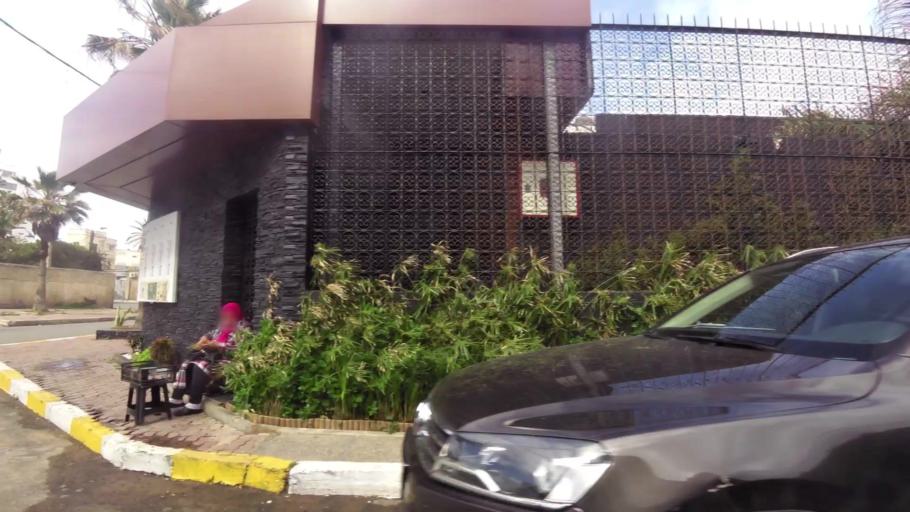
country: MA
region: Grand Casablanca
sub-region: Casablanca
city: Casablanca
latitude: 33.5941
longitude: -7.6767
